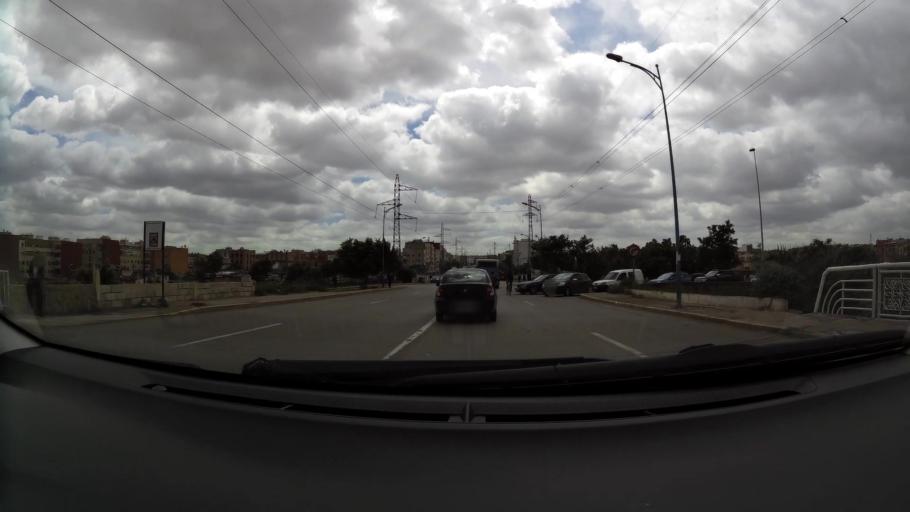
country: MA
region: Grand Casablanca
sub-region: Mediouna
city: Tit Mellil
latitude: 33.5838
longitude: -7.5451
